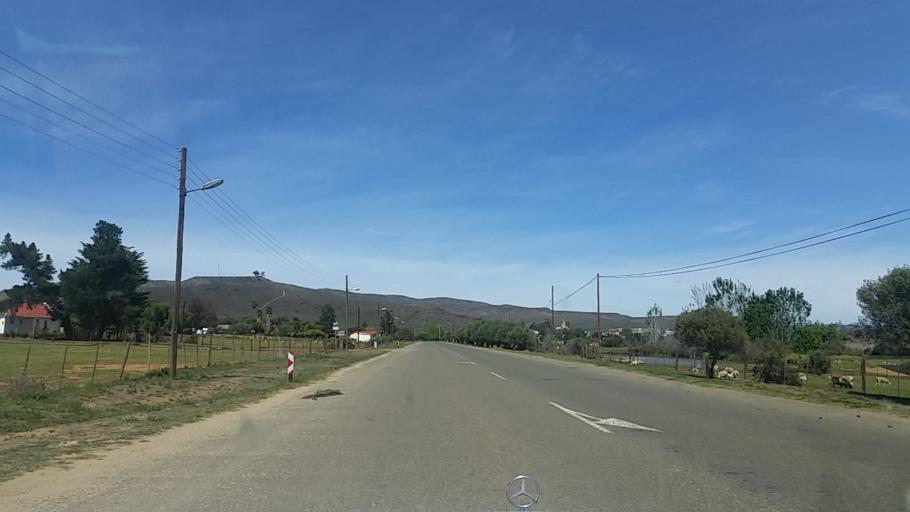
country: ZA
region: Western Cape
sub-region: Eden District Municipality
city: Knysna
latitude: -33.6467
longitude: 23.1363
